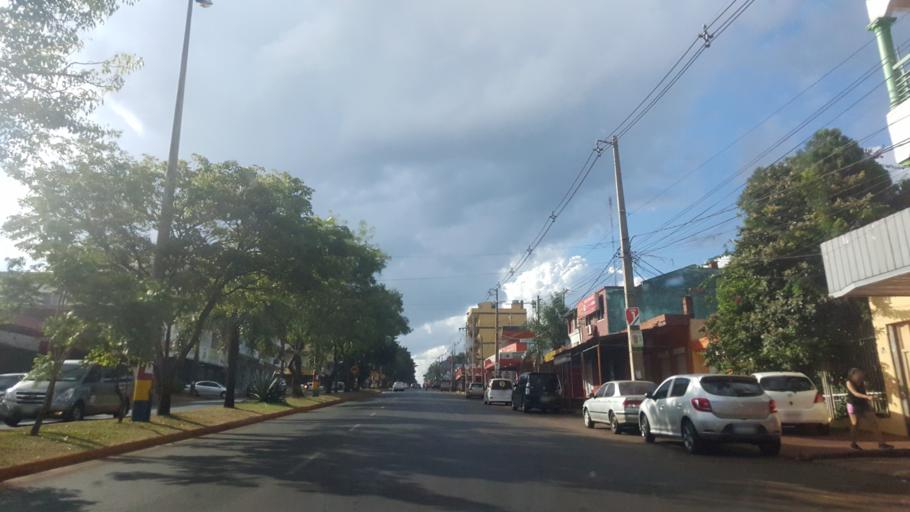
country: PY
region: Itapua
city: Encarnacion
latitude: -27.3335
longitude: -55.8586
